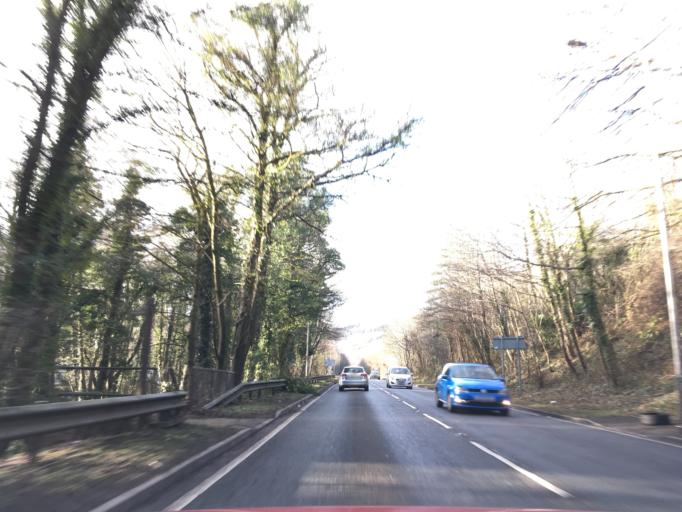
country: GB
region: Wales
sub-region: Torfaen County Borough
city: Pontypool
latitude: 51.6973
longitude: -3.0489
